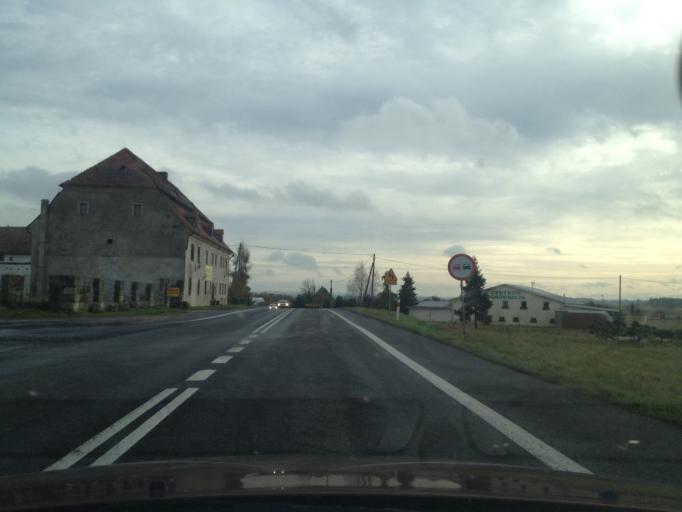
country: PL
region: Lower Silesian Voivodeship
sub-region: Powiat lubanski
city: Pisarzowice
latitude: 51.1379
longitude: 15.2382
